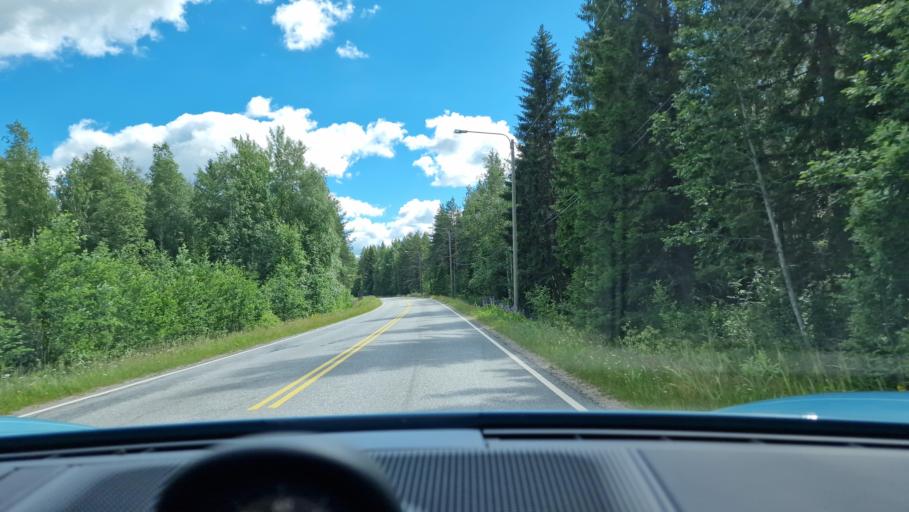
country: FI
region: Southern Ostrobothnia
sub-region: Jaerviseutu
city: Soini
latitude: 62.8369
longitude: 24.3306
